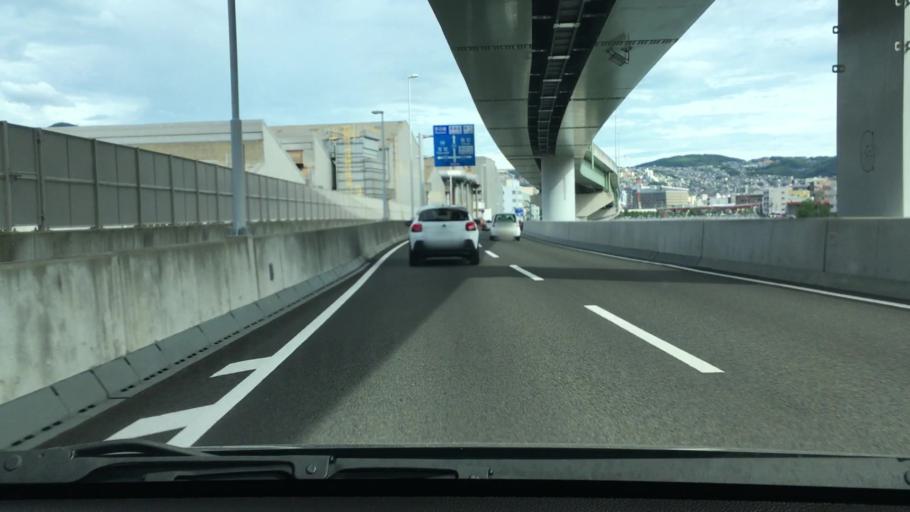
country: JP
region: Nagasaki
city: Nagasaki-shi
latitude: 32.7602
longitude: 129.8623
